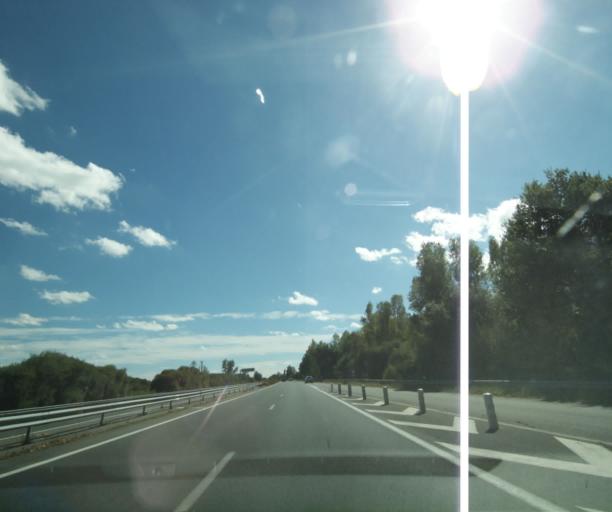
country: FR
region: Aquitaine
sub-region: Departement du Lot-et-Garonne
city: Damazan
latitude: 44.3414
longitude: 0.2516
